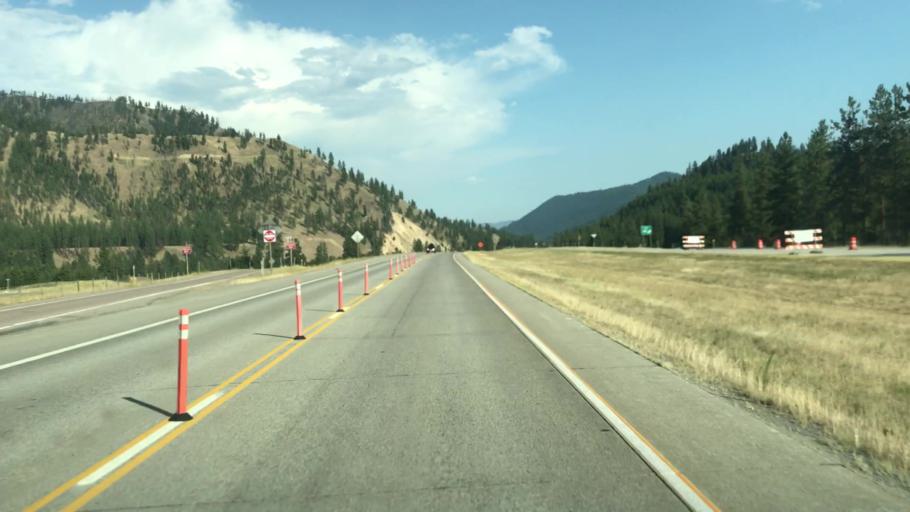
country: US
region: Montana
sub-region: Mineral County
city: Superior
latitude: 47.2281
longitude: -114.9728
